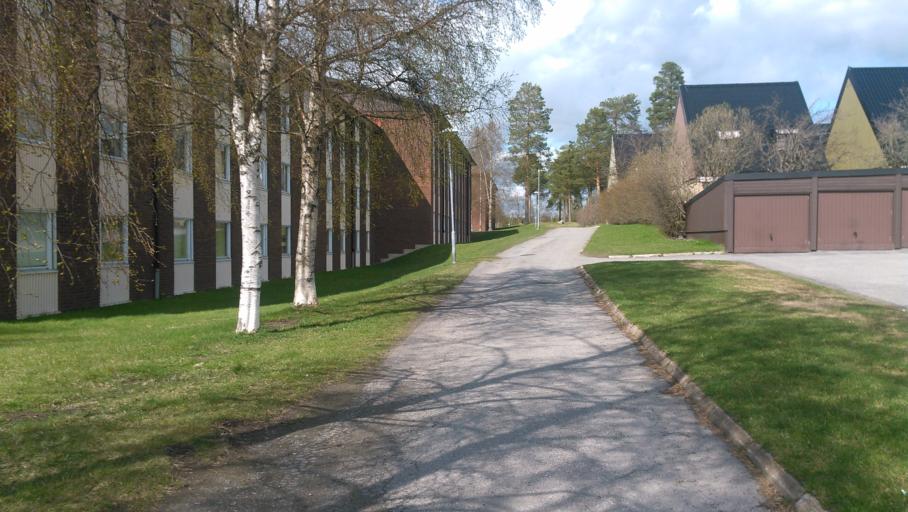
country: SE
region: Vaesterbotten
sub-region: Umea Kommun
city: Umea
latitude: 63.7999
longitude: 20.3167
